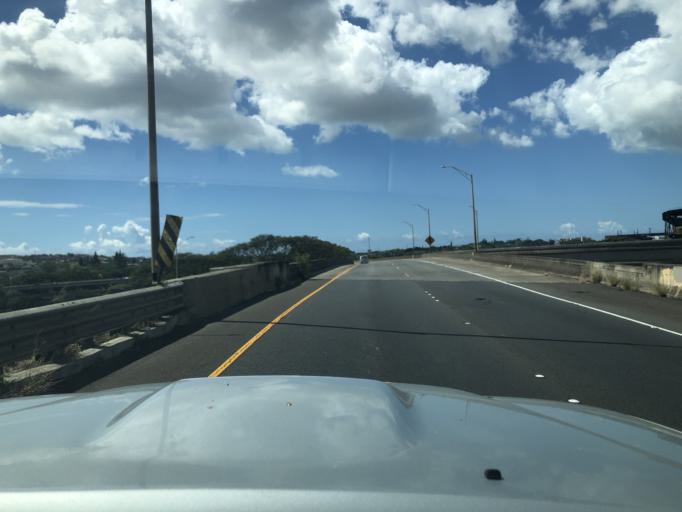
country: US
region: Hawaii
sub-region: Honolulu County
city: Halawa
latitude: 21.3746
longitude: -157.9267
